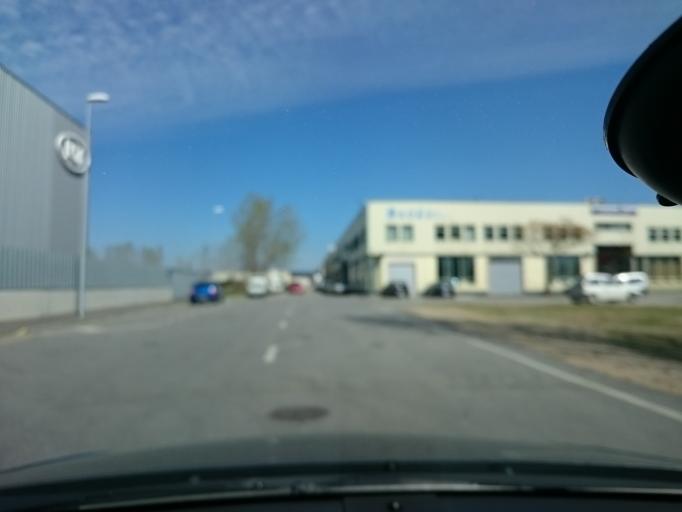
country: ES
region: Castille and Leon
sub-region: Provincia de Leon
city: Camponaraya
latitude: 42.5646
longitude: -6.6409
